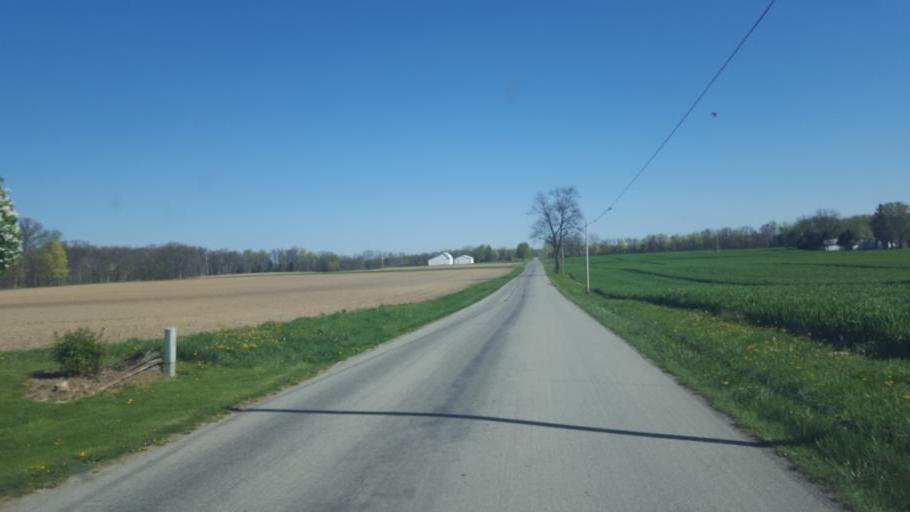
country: US
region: Ohio
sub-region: Wyandot County
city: Upper Sandusky
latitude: 40.8740
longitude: -83.2227
